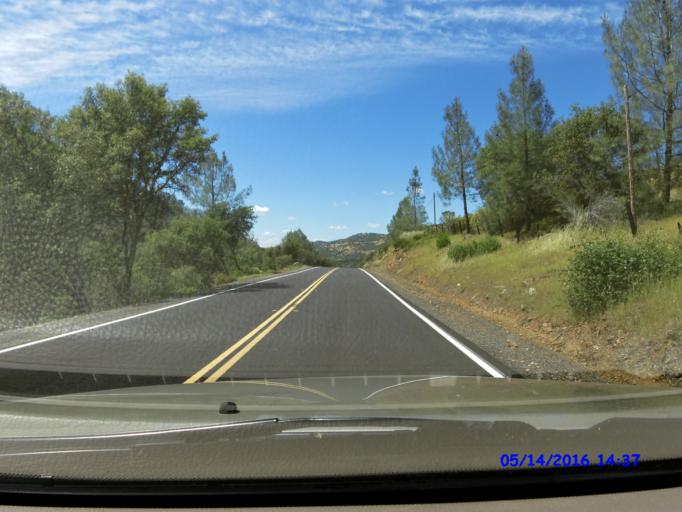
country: US
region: California
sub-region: Tuolumne County
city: Tuolumne City
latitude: 37.7931
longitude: -120.2810
